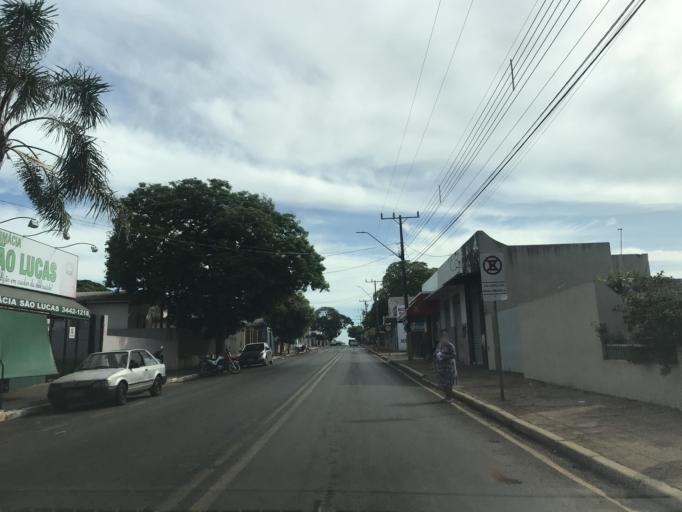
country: BR
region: Parana
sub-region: Paranavai
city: Nova Aurora
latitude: -22.9346
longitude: -52.6862
